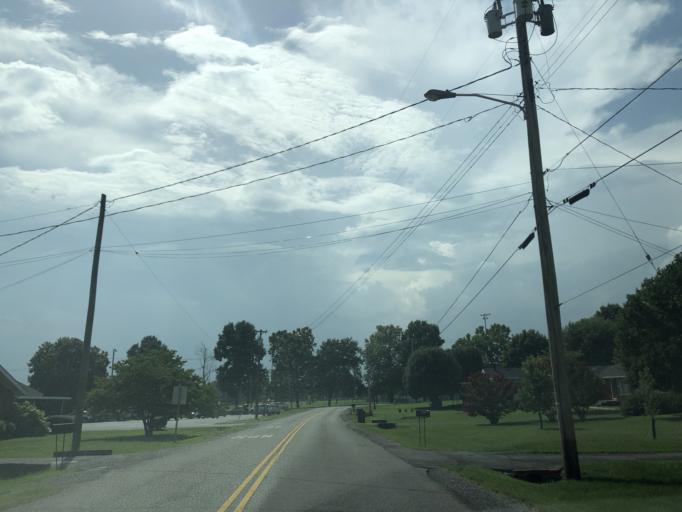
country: US
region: Tennessee
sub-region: Davidson County
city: Lakewood
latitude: 36.1867
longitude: -86.6741
